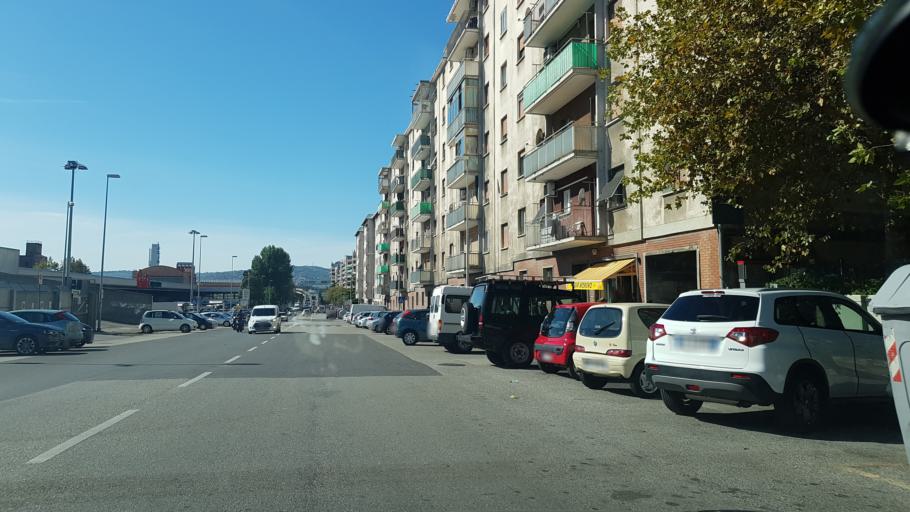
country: IT
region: Friuli Venezia Giulia
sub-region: Provincia di Trieste
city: Trieste
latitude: 45.6236
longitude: 13.7914
